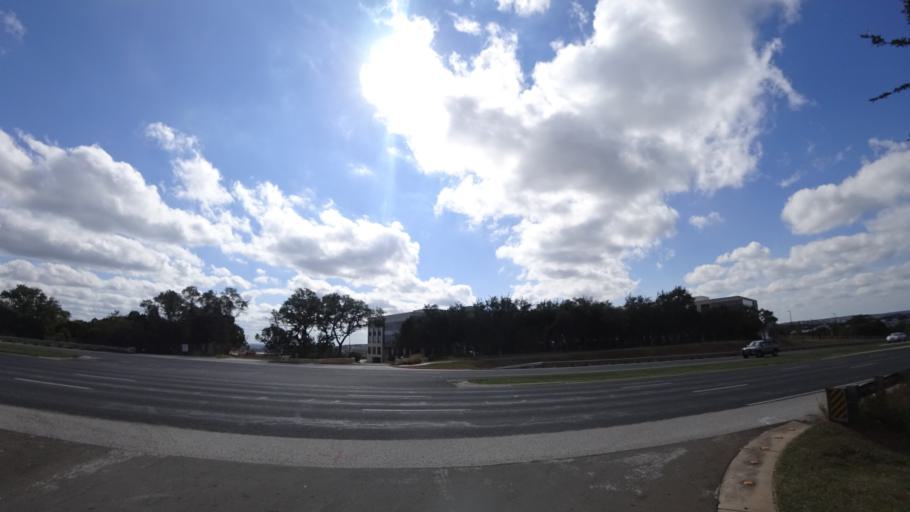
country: US
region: Texas
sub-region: Travis County
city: Barton Creek
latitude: 30.2573
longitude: -97.8709
